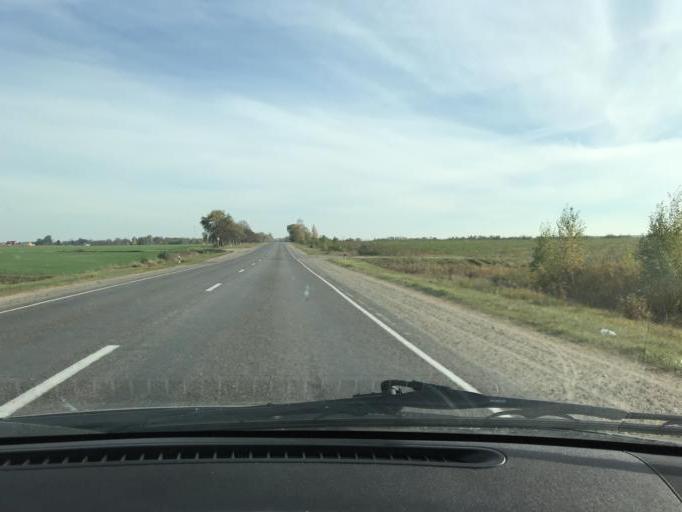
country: BY
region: Brest
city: Asnyezhytsy
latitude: 52.2072
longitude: 26.0531
